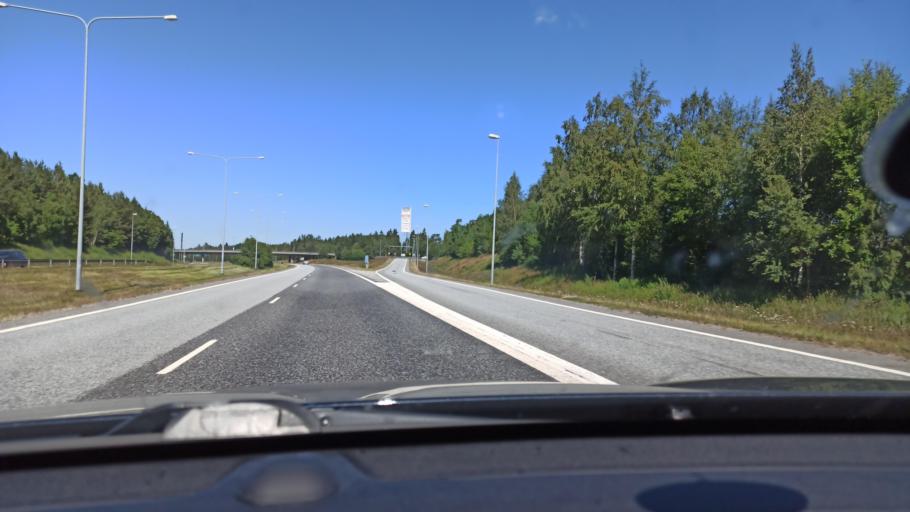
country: FI
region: Ostrobothnia
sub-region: Vaasa
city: Teeriniemi
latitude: 63.0677
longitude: 21.7018
